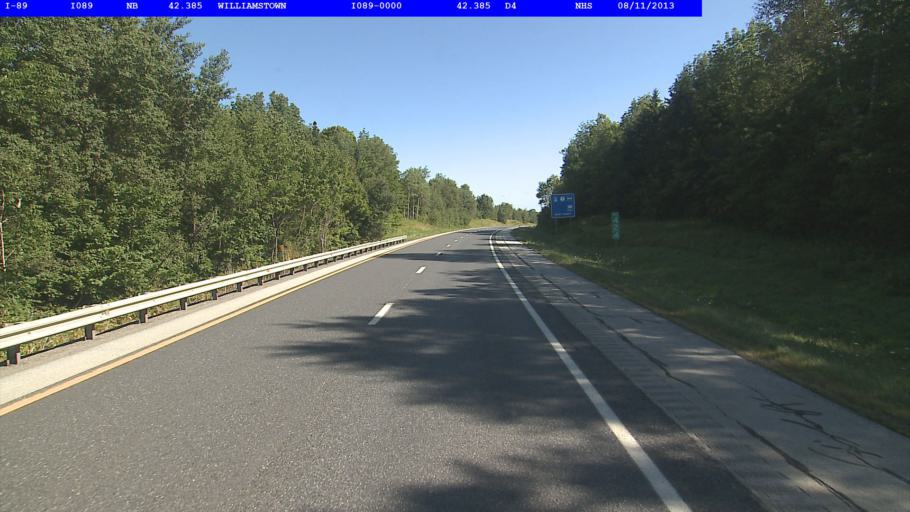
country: US
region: Vermont
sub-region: Washington County
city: Northfield
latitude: 44.1074
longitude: -72.6114
